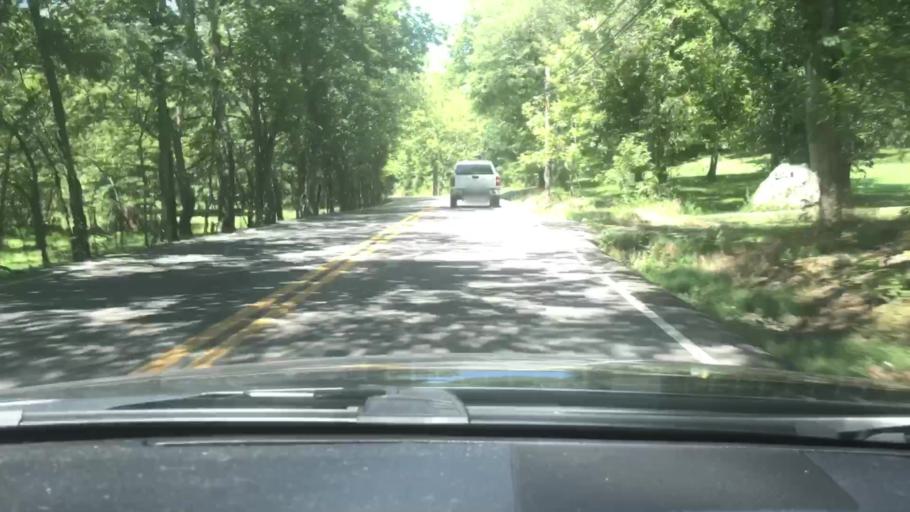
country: US
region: Tennessee
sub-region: Sumner County
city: Gallatin
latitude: 36.4418
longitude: -86.5296
